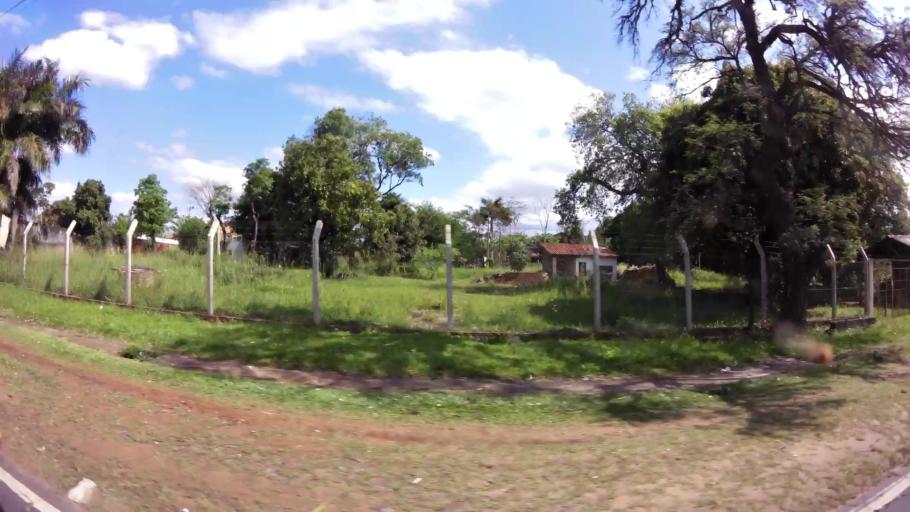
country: PY
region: Central
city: Fernando de la Mora
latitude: -25.2639
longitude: -57.5108
